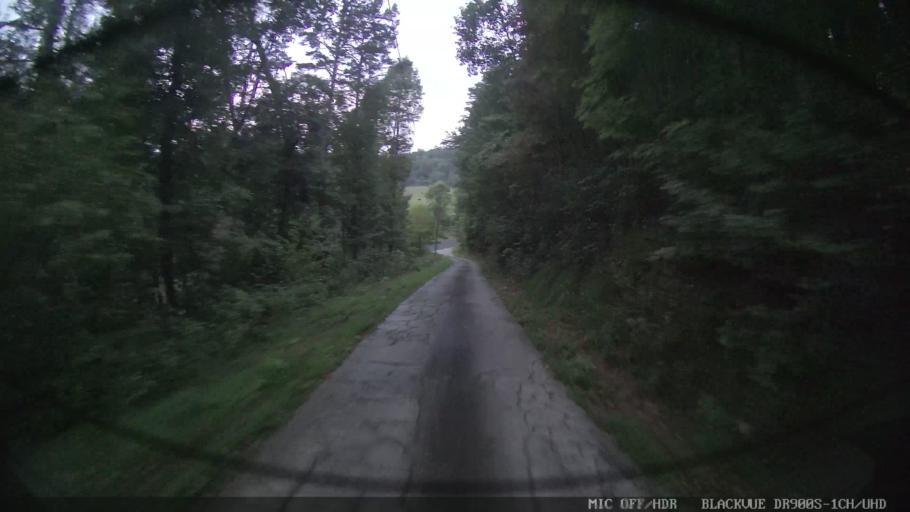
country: US
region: Georgia
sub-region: Gilmer County
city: Ellijay
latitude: 34.6939
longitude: -84.3302
